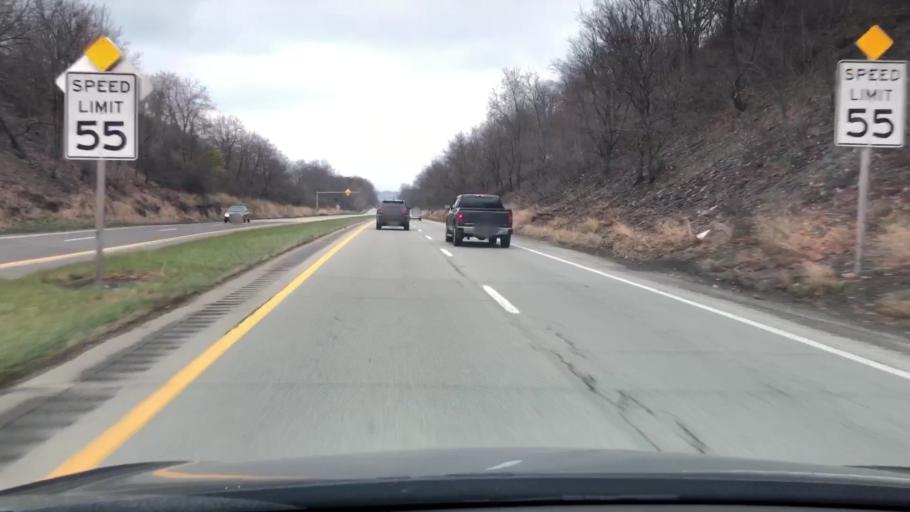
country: US
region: Pennsylvania
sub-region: Westmoreland County
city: Scottdale
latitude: 40.0914
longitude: -79.5588
